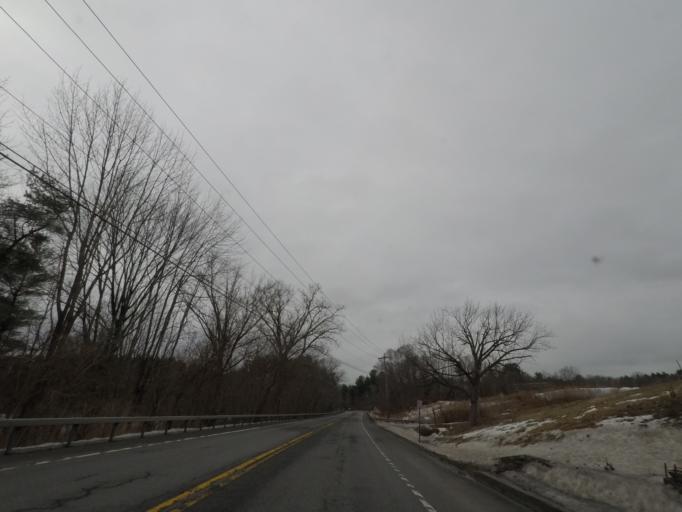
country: US
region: New York
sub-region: Schenectady County
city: Rotterdam
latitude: 42.7301
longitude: -73.9725
